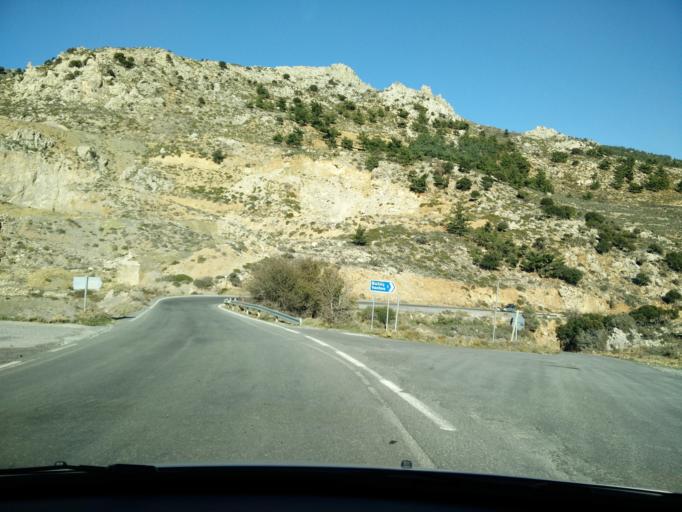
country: GR
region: Crete
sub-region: Nomos Irakleiou
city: Kastelli
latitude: 35.0442
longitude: 25.4289
